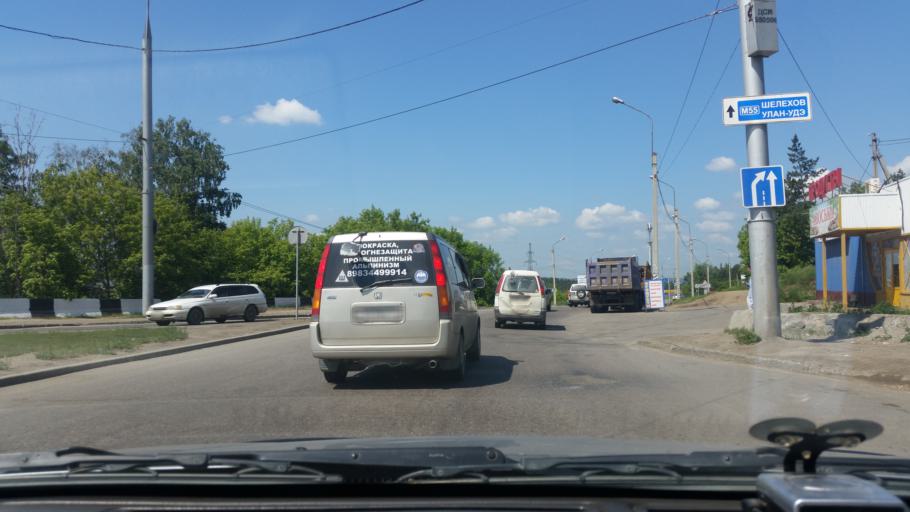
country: RU
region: Irkutsk
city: Smolenshchina
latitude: 52.2598
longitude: 104.1985
